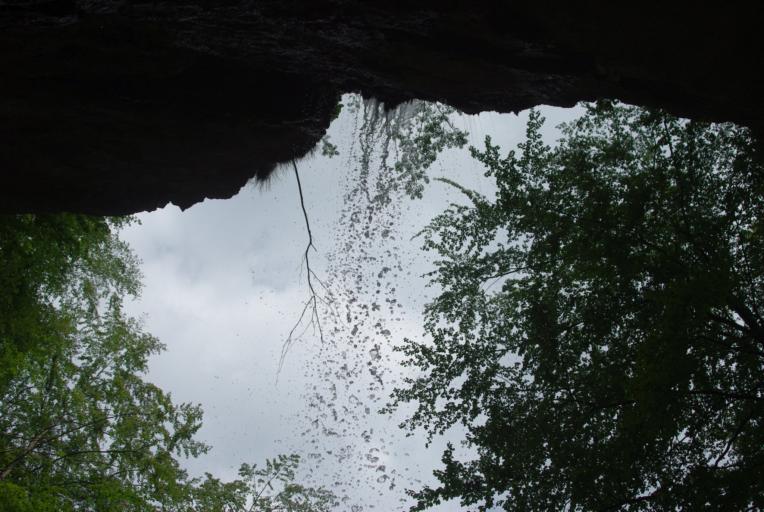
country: RO
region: Bihor
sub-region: Comuna Pietroasa
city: Pietroasa
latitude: 46.6014
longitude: 22.6660
